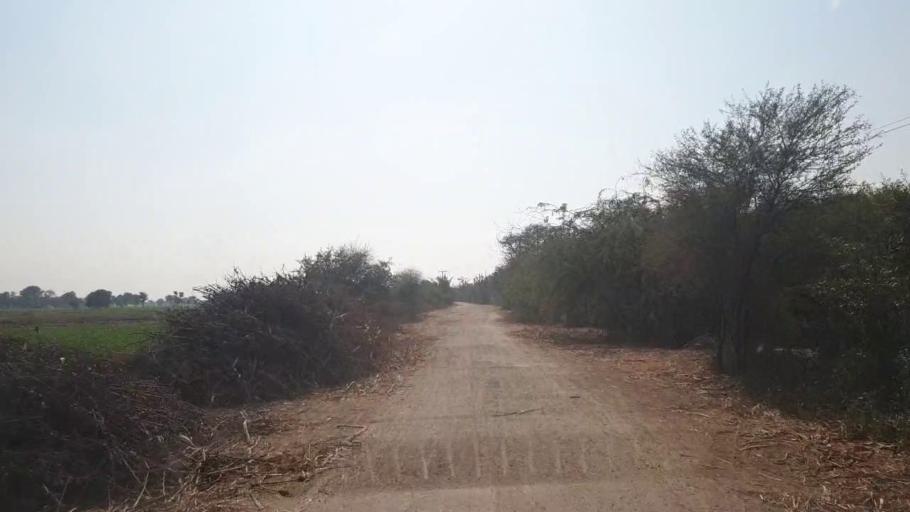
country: PK
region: Sindh
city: Shahdadpur
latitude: 26.0455
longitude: 68.4630
